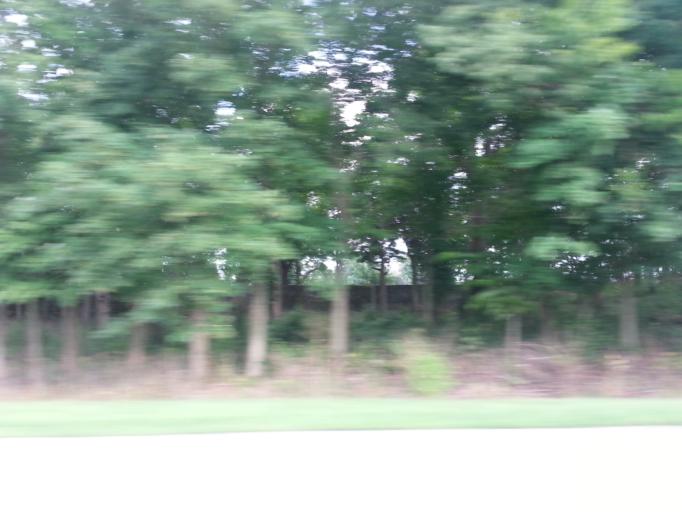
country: US
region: Kentucky
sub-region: Fayette County
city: Lexington-Fayette
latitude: 38.1113
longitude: -84.4029
